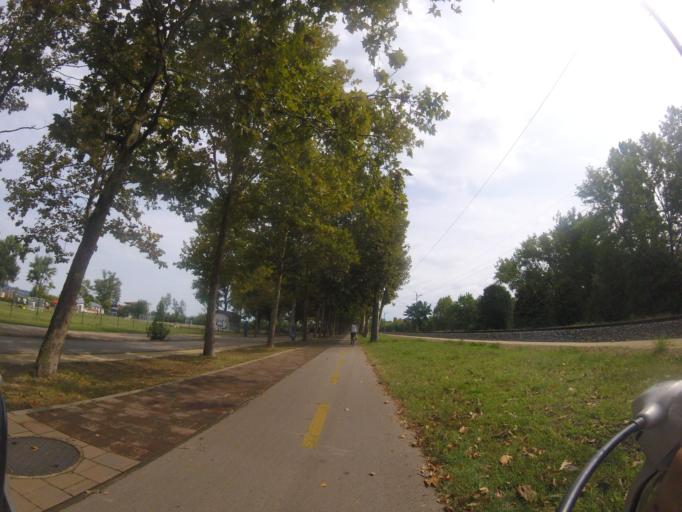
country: HU
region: Somogy
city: Balatonfoldvar
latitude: 46.8594
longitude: 17.8929
